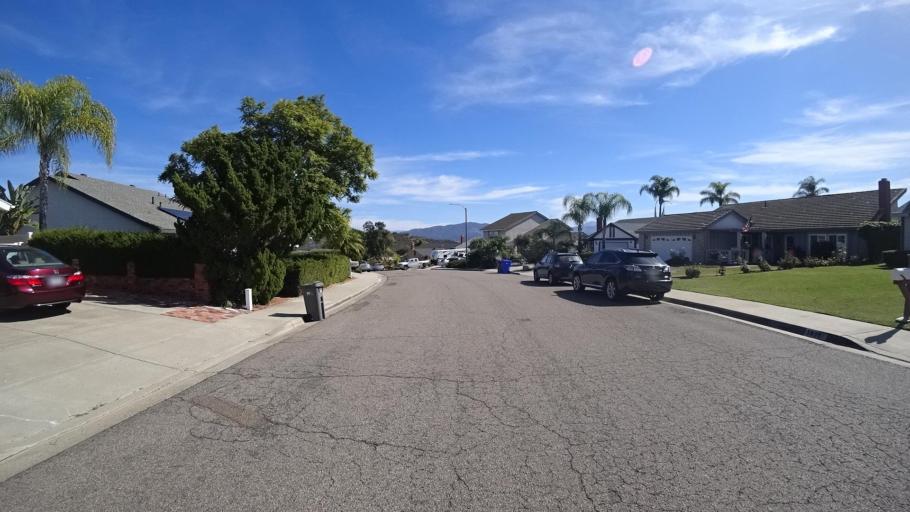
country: US
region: California
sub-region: San Diego County
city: Rancho San Diego
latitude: 32.7493
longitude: -116.9517
